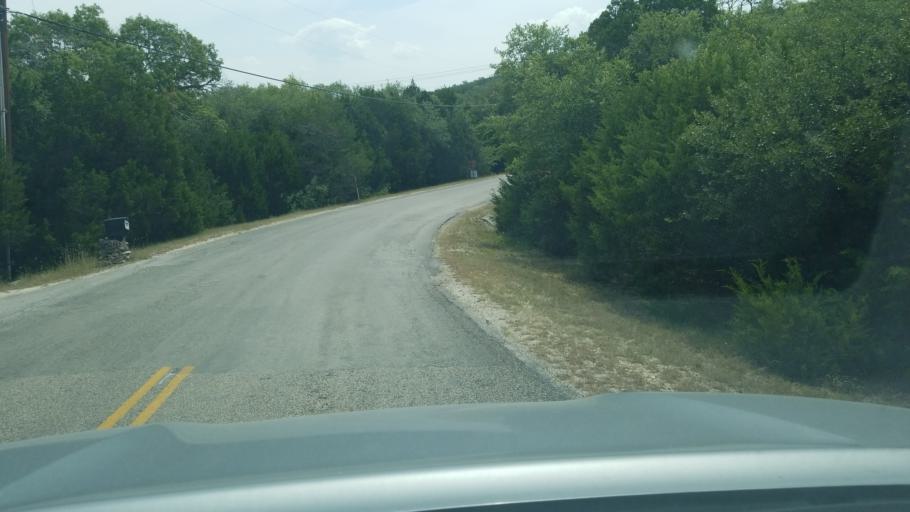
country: US
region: Texas
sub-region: Comal County
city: Bulverde
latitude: 29.7834
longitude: -98.4249
